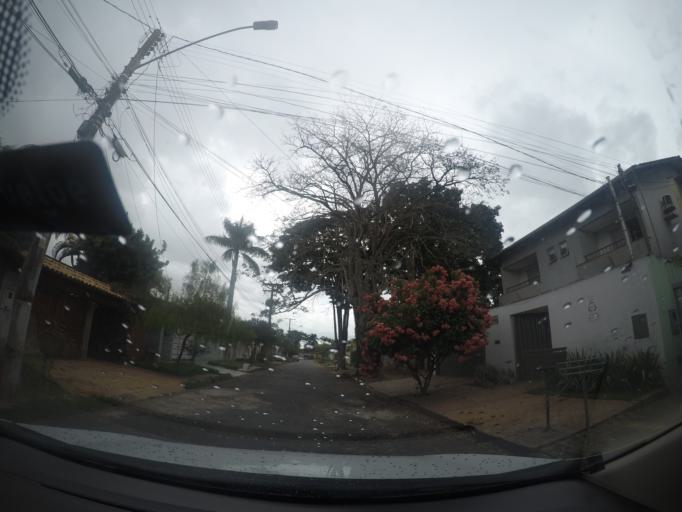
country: BR
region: Goias
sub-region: Goiania
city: Goiania
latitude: -16.6506
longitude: -49.2361
